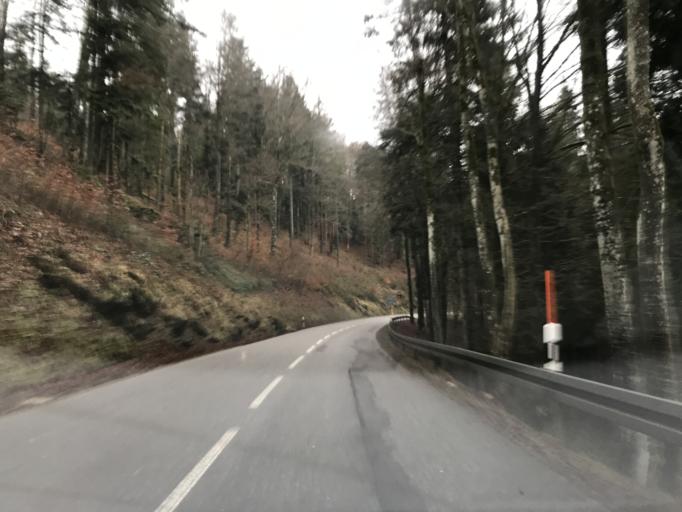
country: DE
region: Baden-Wuerttemberg
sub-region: Freiburg Region
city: Rickenbach
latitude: 47.6146
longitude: 7.9758
